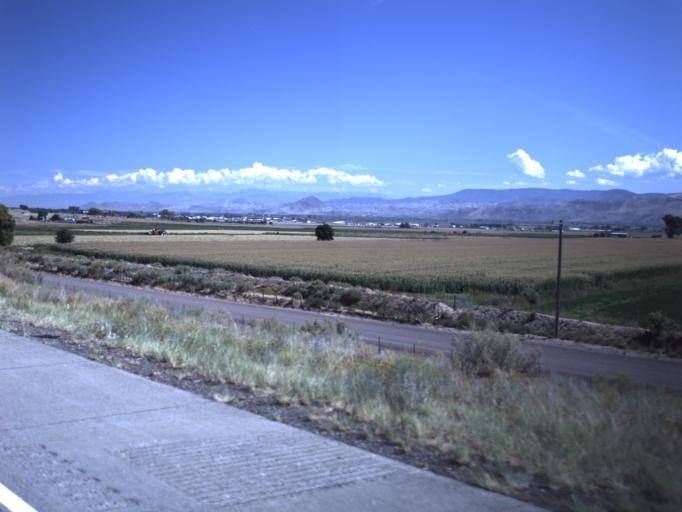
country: US
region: Utah
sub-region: Sevier County
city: Richfield
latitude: 38.7223
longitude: -112.1311
